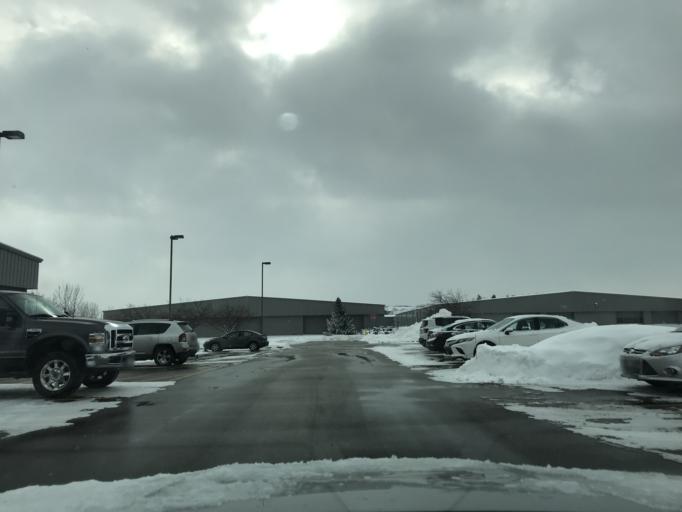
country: US
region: Wisconsin
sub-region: Dane County
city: Sun Prairie
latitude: 43.1609
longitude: -89.2830
